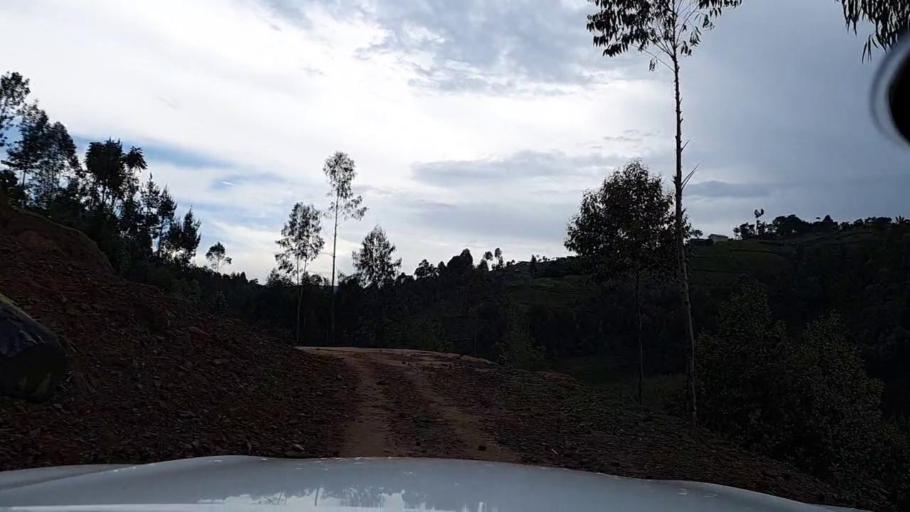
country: BI
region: Kayanza
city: Kayanza
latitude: -2.7744
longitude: 29.4469
